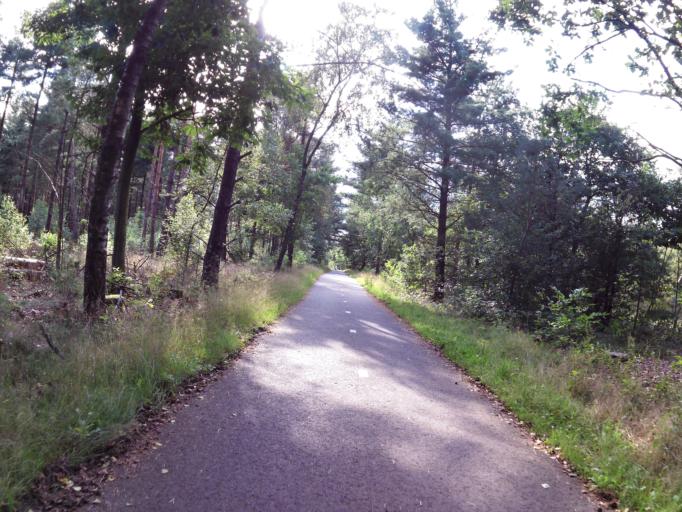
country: NL
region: Gelderland
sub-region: Gemeente Rozendaal
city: Rozendaal
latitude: 52.0381
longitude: 5.9264
